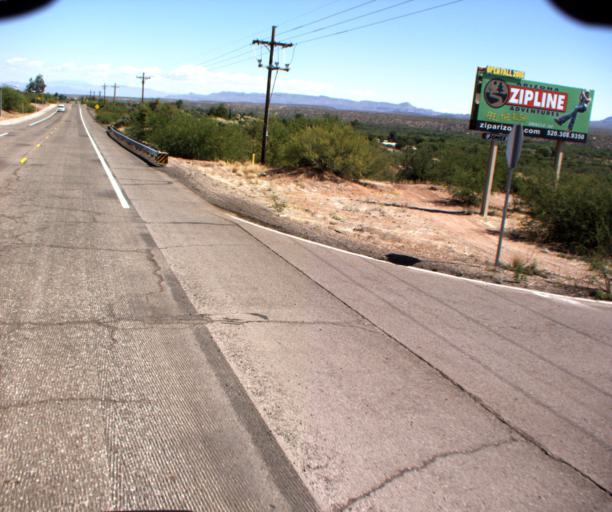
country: US
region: Arizona
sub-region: Pinal County
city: Mammoth
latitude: 32.7259
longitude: -110.6458
